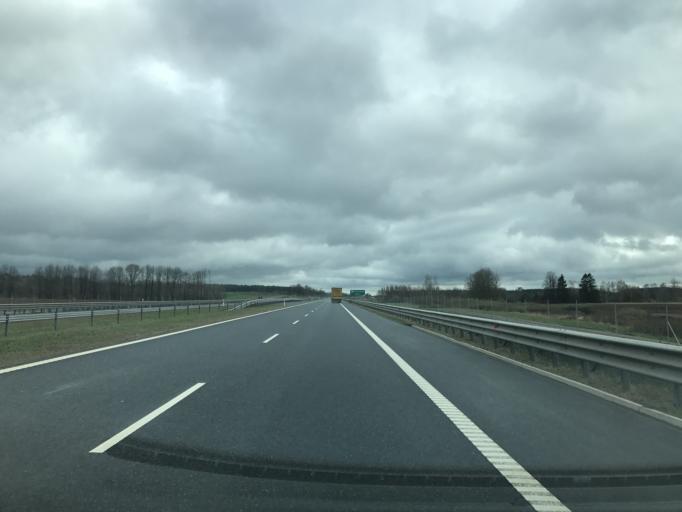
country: PL
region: Warmian-Masurian Voivodeship
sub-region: Powiat olsztynski
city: Olsztynek
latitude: 53.5615
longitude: 20.2654
